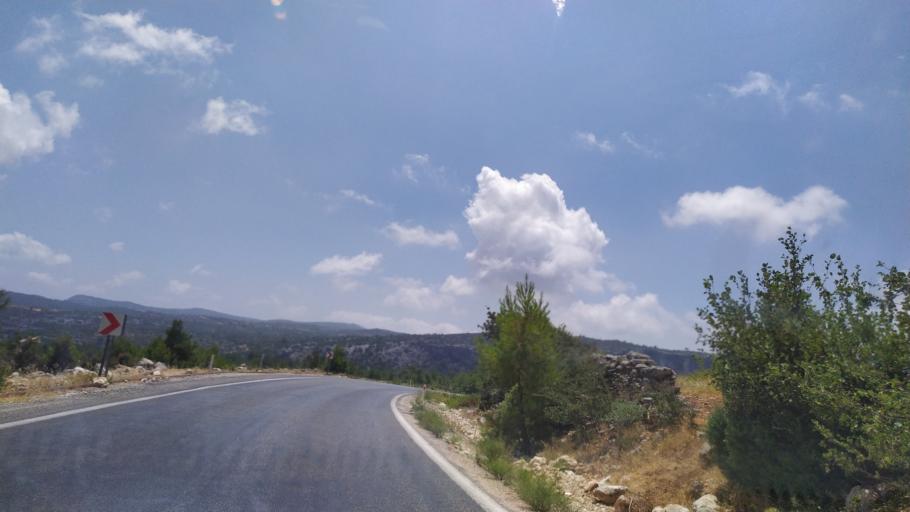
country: TR
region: Mersin
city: Gulnar
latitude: 36.2806
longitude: 33.3890
